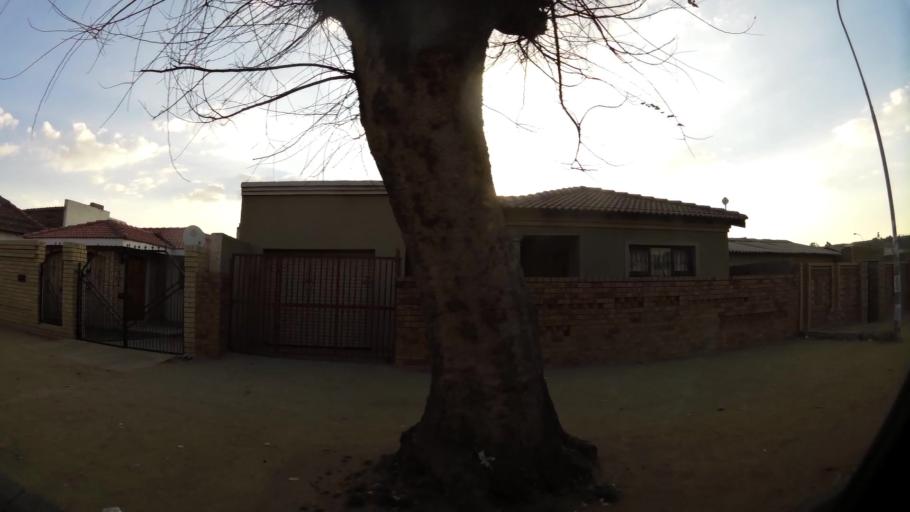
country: ZA
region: Gauteng
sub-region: City of Johannesburg Metropolitan Municipality
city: Roodepoort
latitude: -26.2105
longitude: 27.8952
